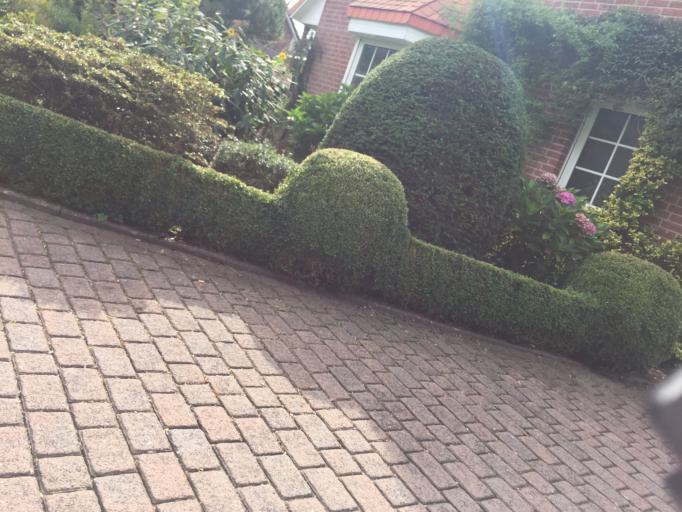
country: DE
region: Schleswig-Holstein
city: Munsterdorf
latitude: 53.9248
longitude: 9.5409
